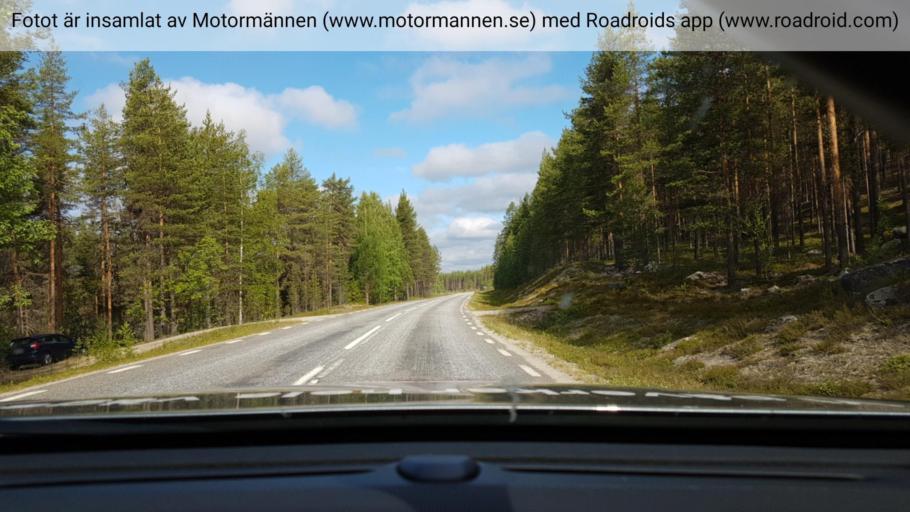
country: SE
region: Vaesterbotten
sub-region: Lycksele Kommun
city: Lycksele
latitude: 64.7808
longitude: 18.9997
